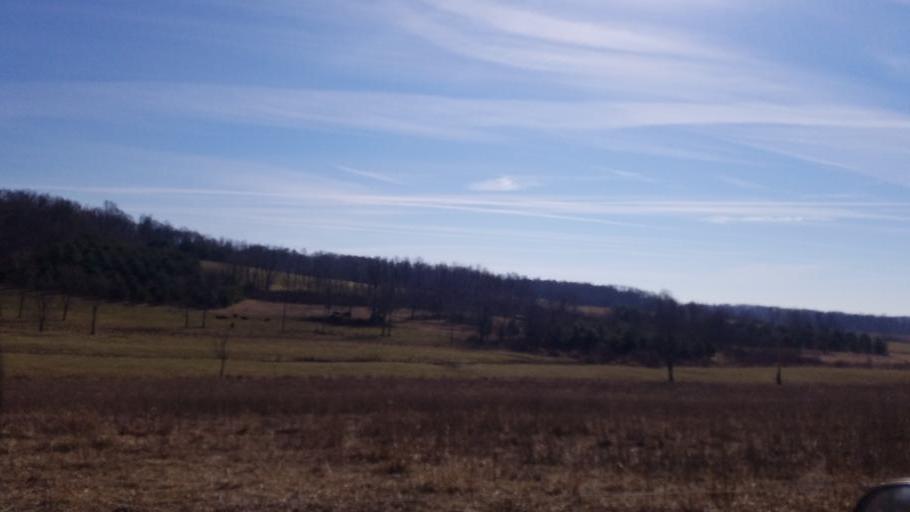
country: US
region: Ohio
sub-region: Knox County
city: Fredericktown
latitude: 40.5184
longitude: -82.4533
